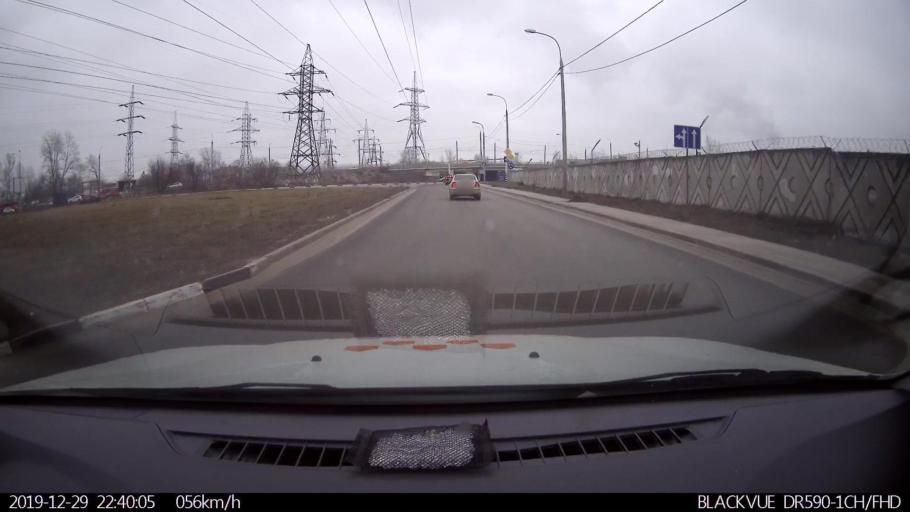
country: RU
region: Nizjnij Novgorod
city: Nizhniy Novgorod
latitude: 56.2619
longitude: 43.9053
